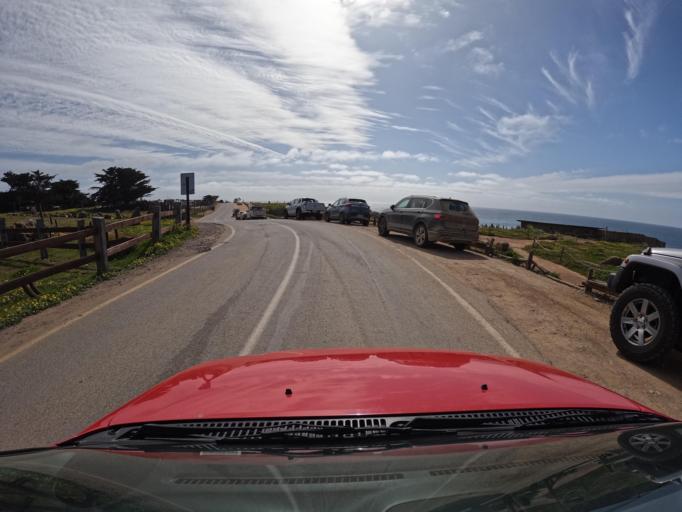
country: CL
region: O'Higgins
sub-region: Provincia de Colchagua
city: Santa Cruz
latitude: -34.4257
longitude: -72.0451
